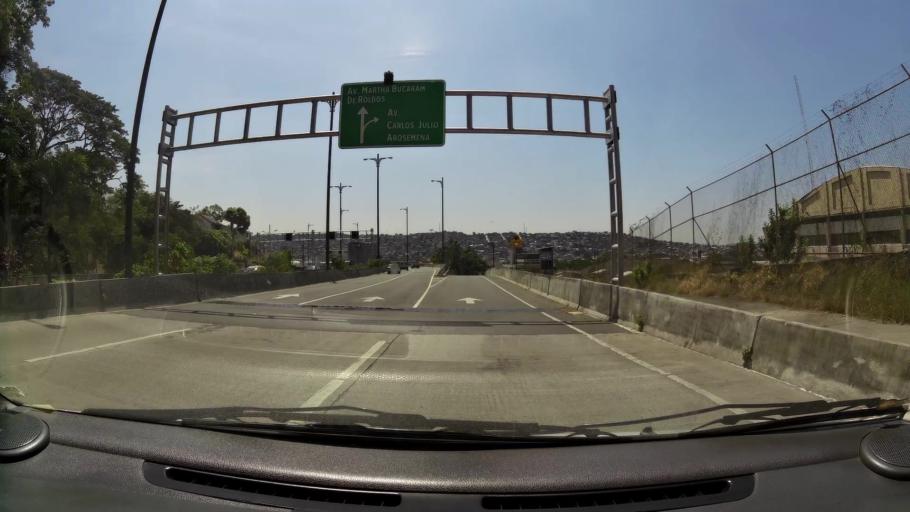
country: EC
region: Guayas
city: Guayaquil
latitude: -2.1648
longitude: -79.9268
